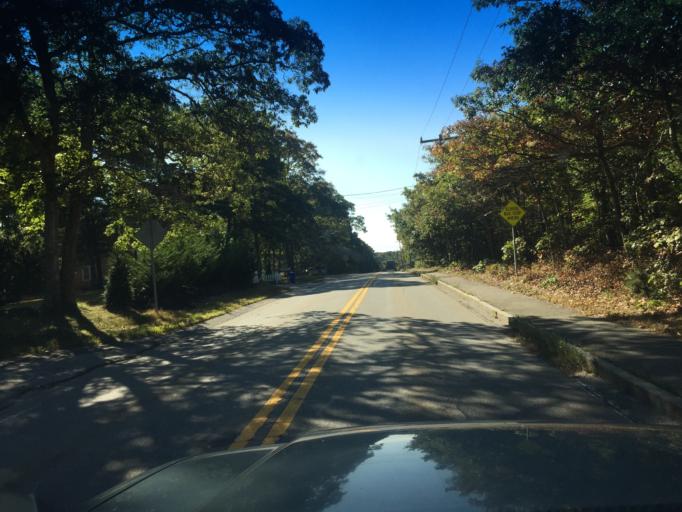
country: US
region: Massachusetts
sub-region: Barnstable County
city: North Falmouth
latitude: 41.6537
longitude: -70.6124
